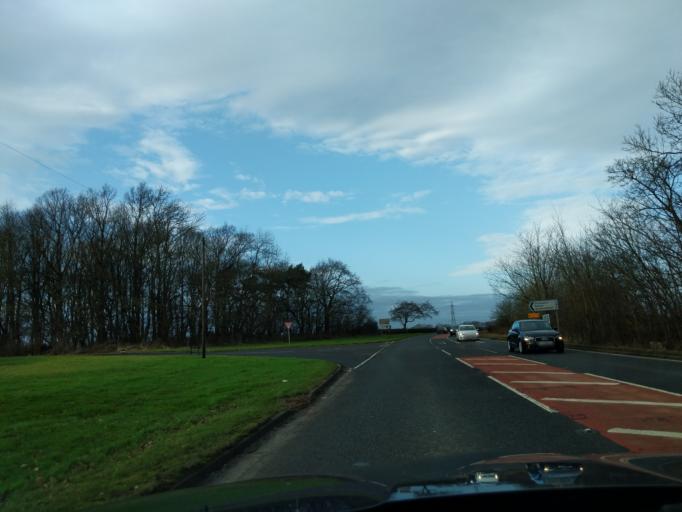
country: GB
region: England
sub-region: Northumberland
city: Ponteland
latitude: 55.0549
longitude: -1.7631
